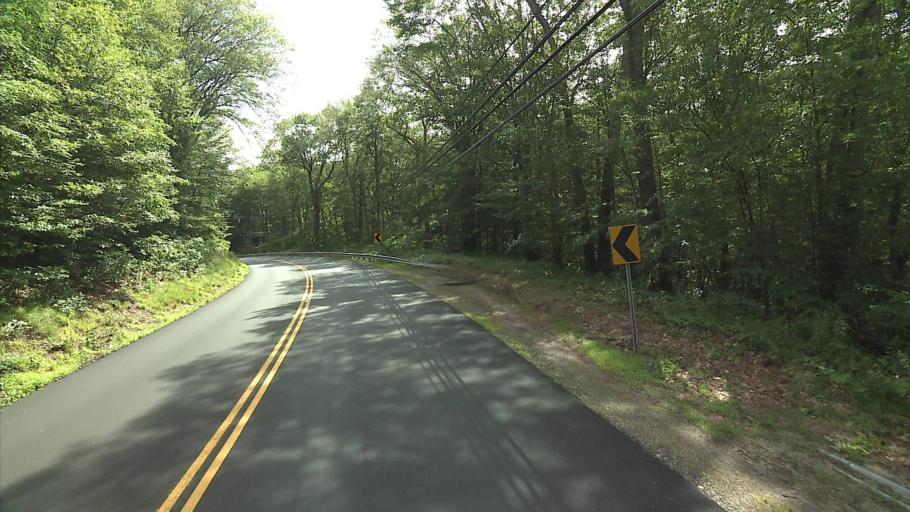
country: US
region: Connecticut
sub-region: Windham County
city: South Woodstock
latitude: 41.9473
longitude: -72.0218
